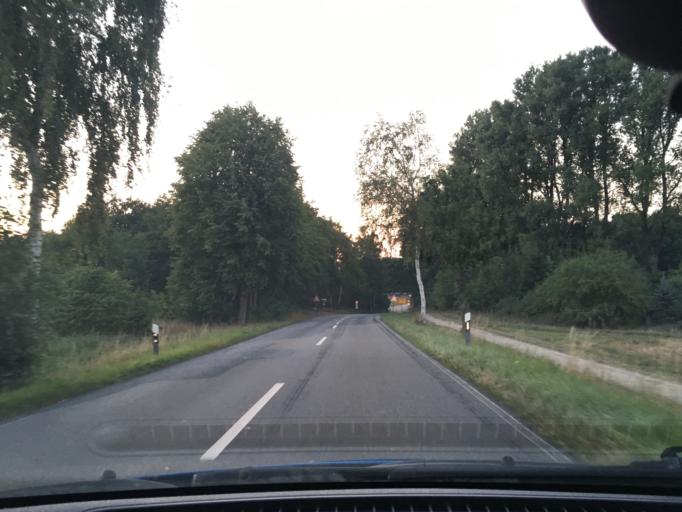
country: DE
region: Lower Saxony
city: Embsen
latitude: 53.1559
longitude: 10.3480
